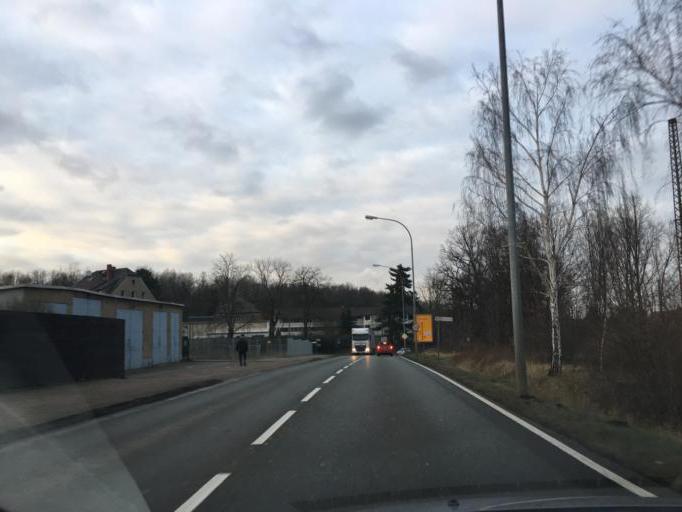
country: DE
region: Saxony
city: Borna
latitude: 51.1181
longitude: 12.4847
